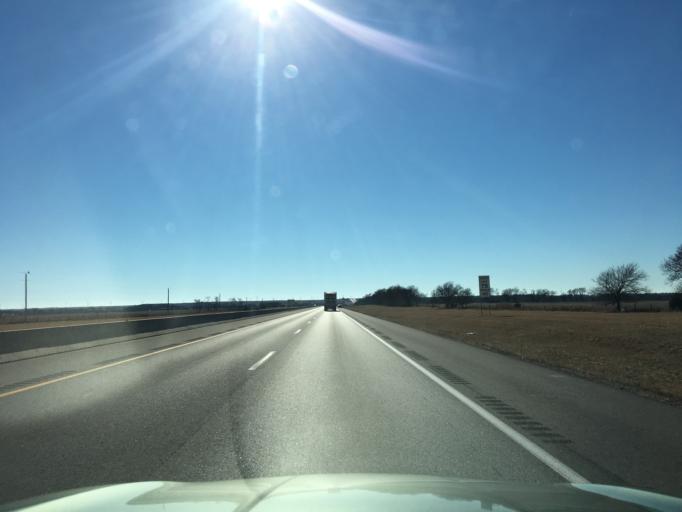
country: US
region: Kansas
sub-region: Sumner County
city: Wellington
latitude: 37.2296
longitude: -97.3388
